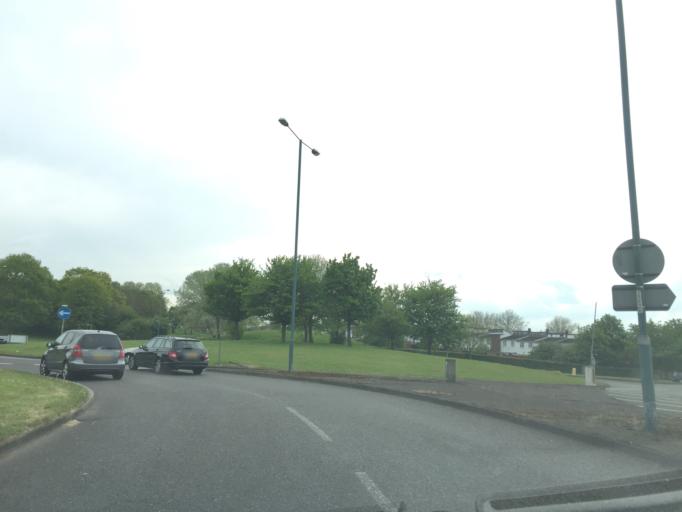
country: GB
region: England
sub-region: Essex
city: Roydon
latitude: 51.7540
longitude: 0.0738
